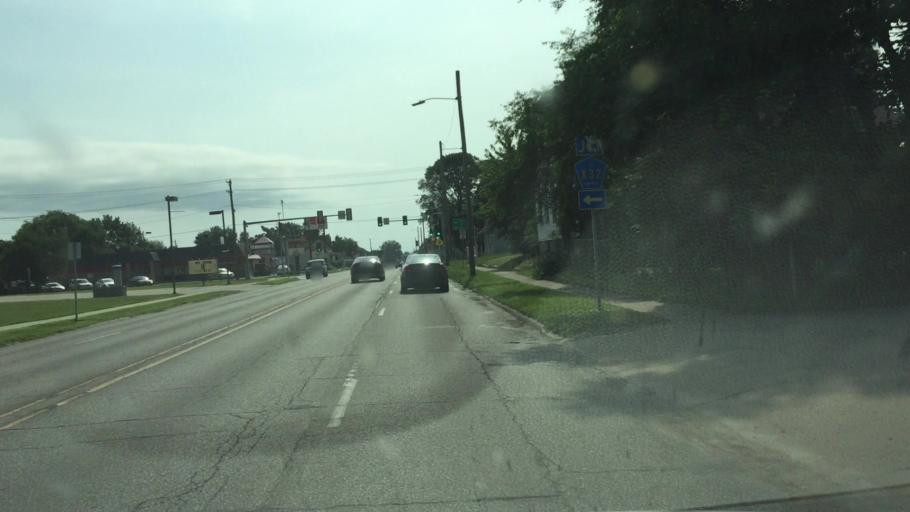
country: US
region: Iowa
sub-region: Lee County
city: Fort Madison
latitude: 40.6301
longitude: -91.3259
